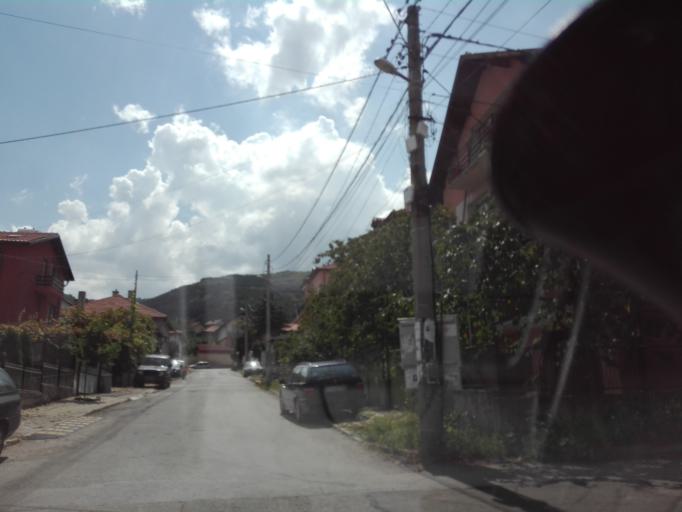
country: BG
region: Sofiya
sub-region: Obshtina Elin Pelin
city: Elin Pelin
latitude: 42.6025
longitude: 23.4842
